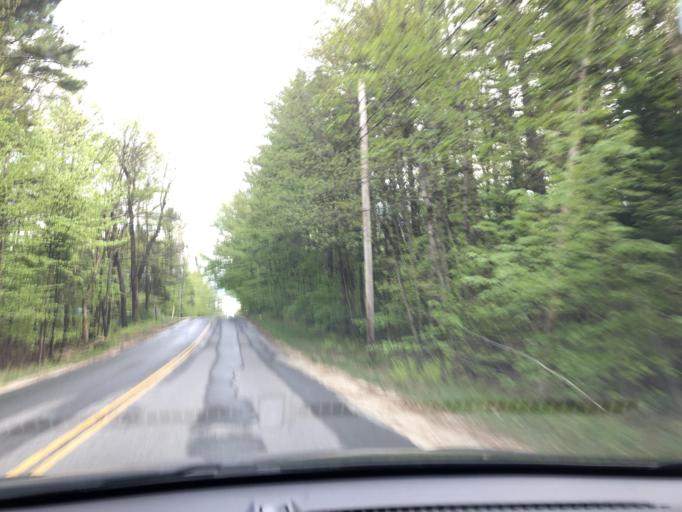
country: US
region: New Hampshire
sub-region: Merrimack County
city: New London
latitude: 43.4160
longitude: -72.0058
